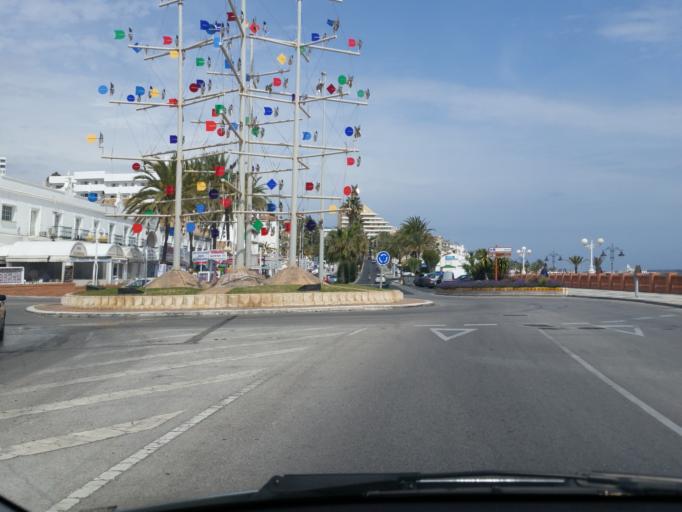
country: ES
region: Andalusia
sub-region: Provincia de Malaga
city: Torremolinos
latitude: 36.5904
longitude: -4.5274
